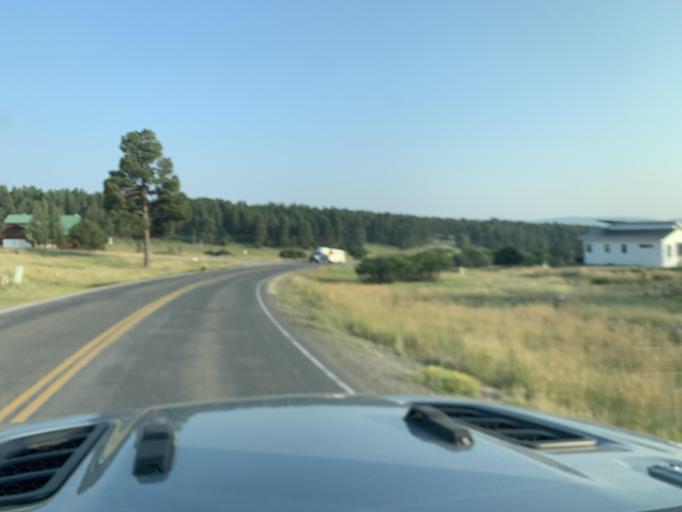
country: US
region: Colorado
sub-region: Archuleta County
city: Pagosa Springs
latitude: 37.2868
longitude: -107.0958
